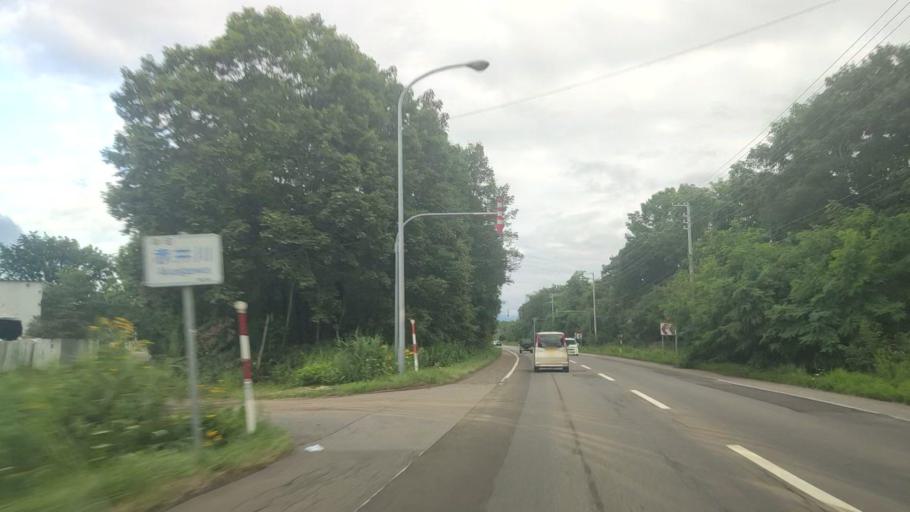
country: JP
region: Hokkaido
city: Nanae
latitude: 42.0236
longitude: 140.6139
